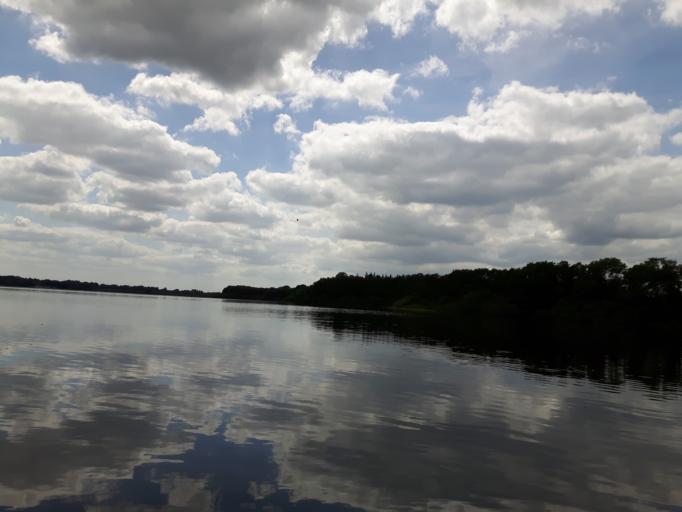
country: DE
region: Schleswig-Holstein
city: Muhbrook
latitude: 54.1502
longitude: 10.0047
